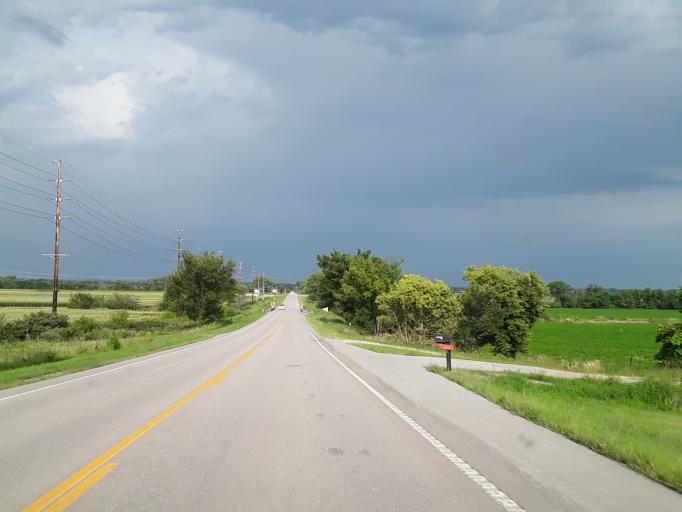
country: US
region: Nebraska
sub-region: Saunders County
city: Ashland
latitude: 41.0886
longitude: -96.3831
